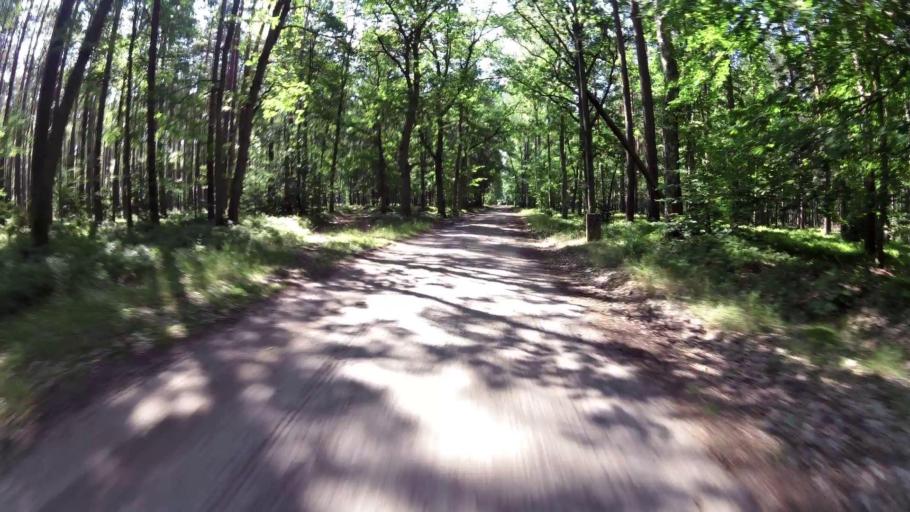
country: PL
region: West Pomeranian Voivodeship
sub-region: Powiat drawski
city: Czaplinek
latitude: 53.4268
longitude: 16.2666
